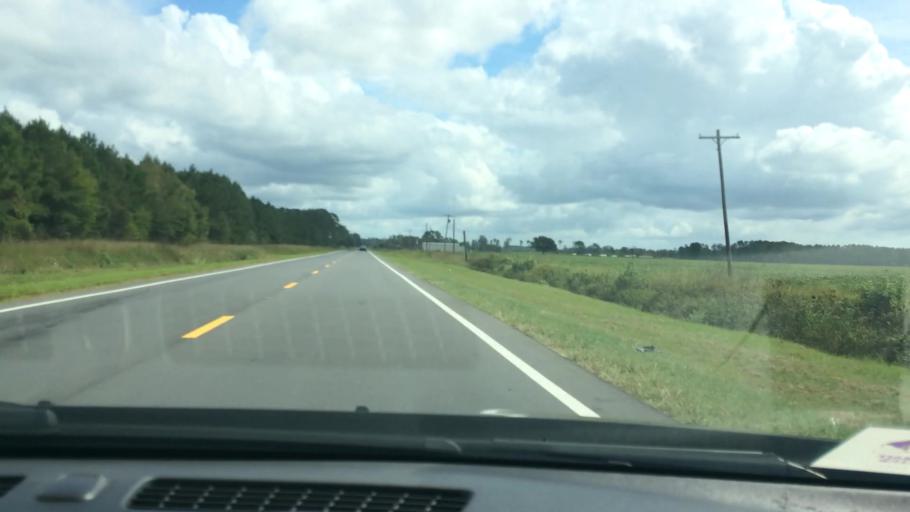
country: US
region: North Carolina
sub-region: Pitt County
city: Farmville
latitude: 35.5760
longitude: -77.5831
